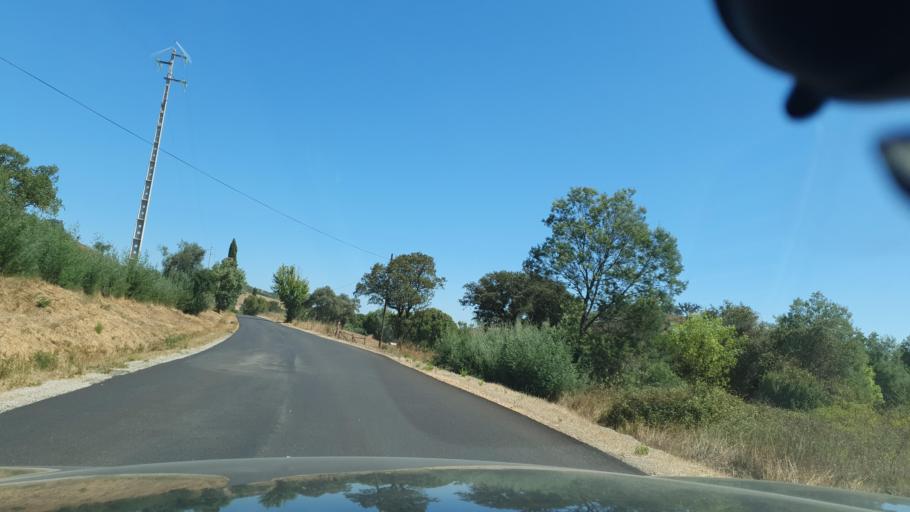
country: PT
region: Faro
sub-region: Monchique
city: Monchique
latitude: 37.4780
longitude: -8.4892
